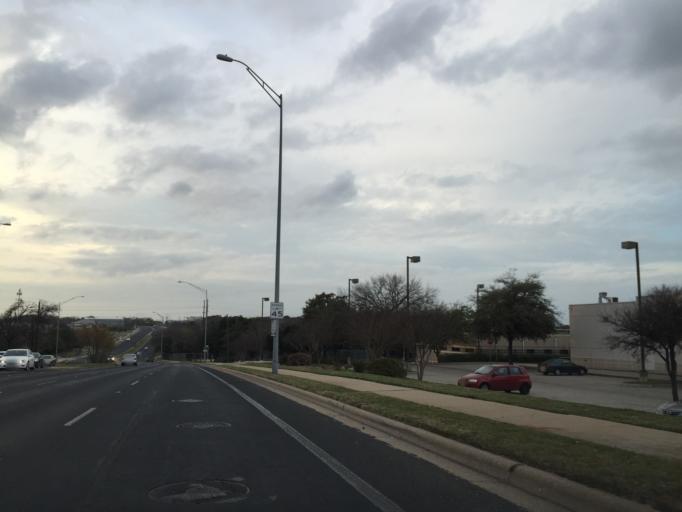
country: US
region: Texas
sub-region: Travis County
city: Wells Branch
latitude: 30.3821
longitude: -97.6866
